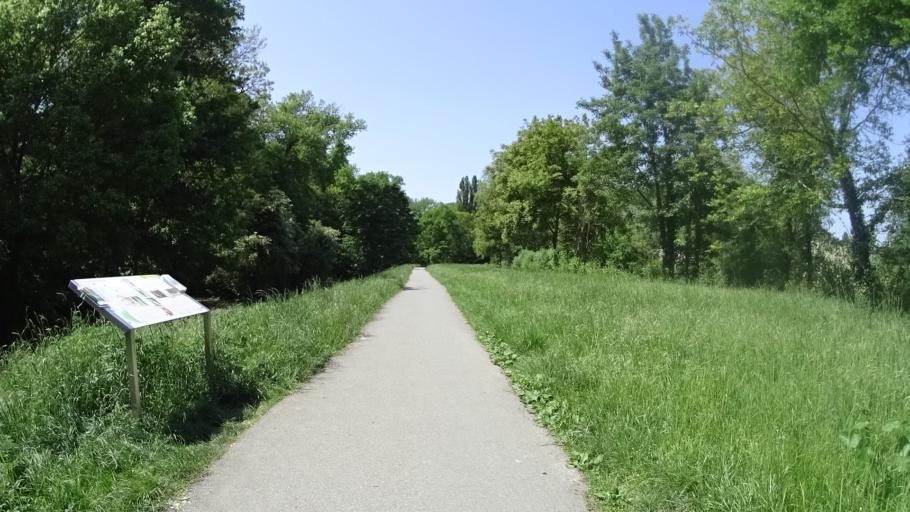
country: DE
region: Rheinland-Pfalz
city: Altrip
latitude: 49.4454
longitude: 8.4663
